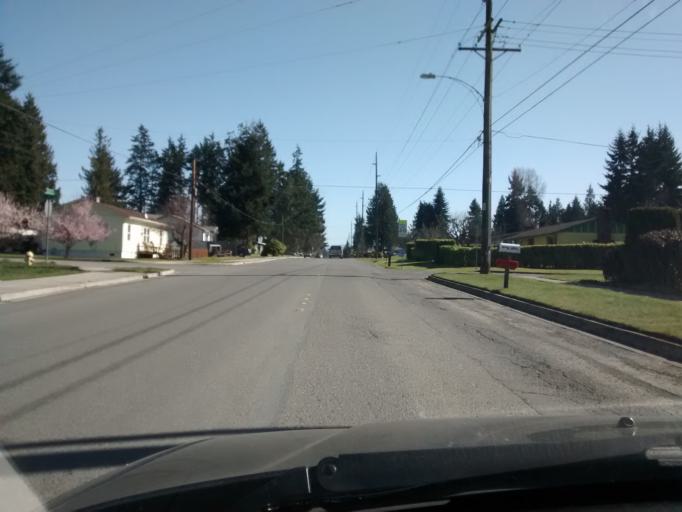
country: US
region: Washington
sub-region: Clallam County
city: Port Angeles
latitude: 48.1160
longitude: -123.4698
